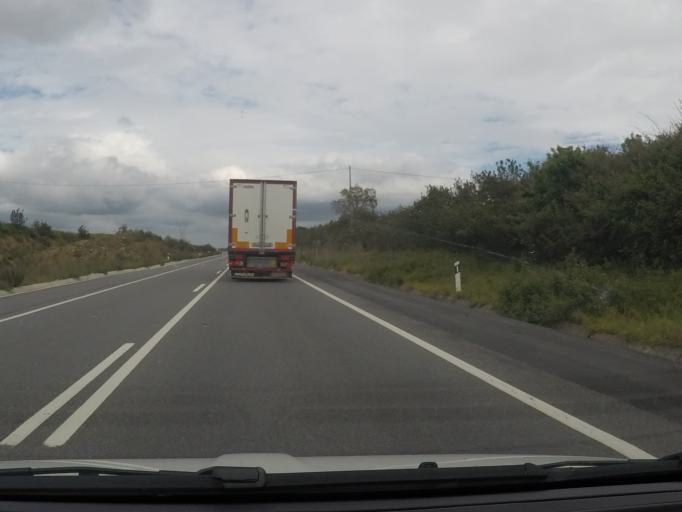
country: PT
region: Setubal
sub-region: Santiago do Cacem
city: Santiago do Cacem
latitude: 38.0709
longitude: -8.6629
